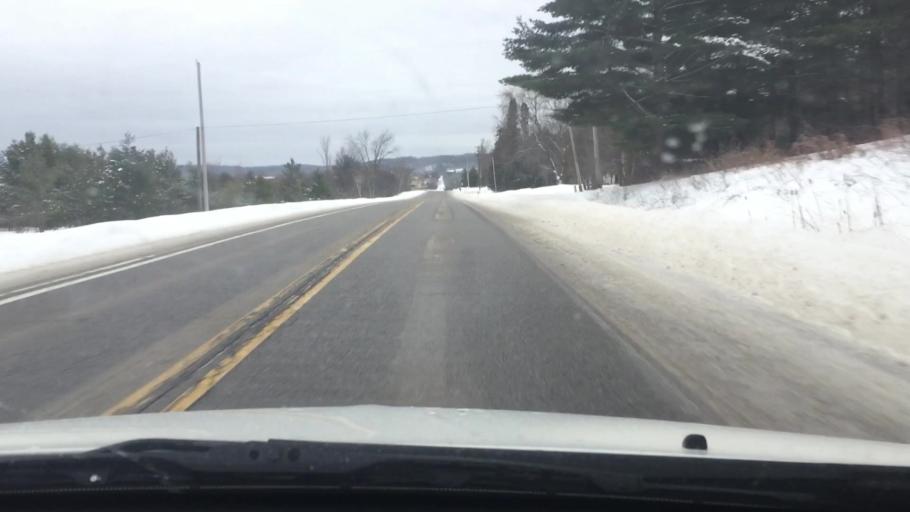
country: US
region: Michigan
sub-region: Charlevoix County
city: East Jordan
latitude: 45.1431
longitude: -85.1398
